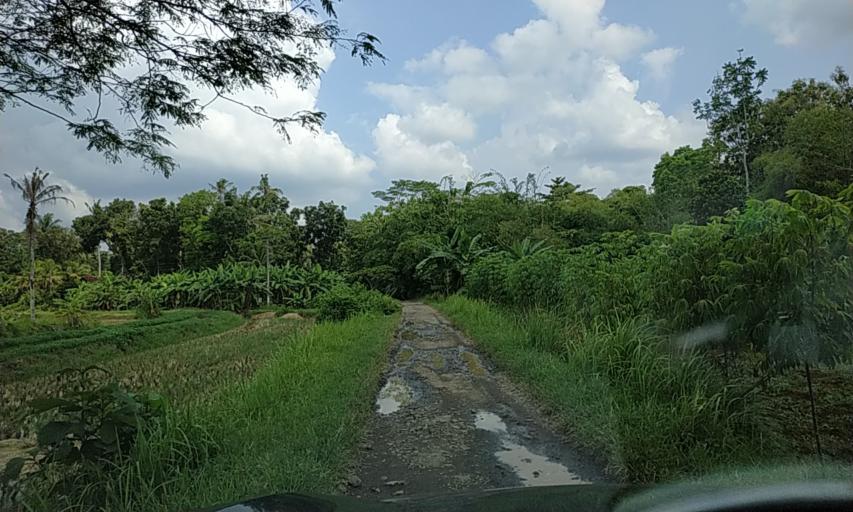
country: ID
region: Central Java
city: Bakung
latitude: -7.3404
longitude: 108.6678
